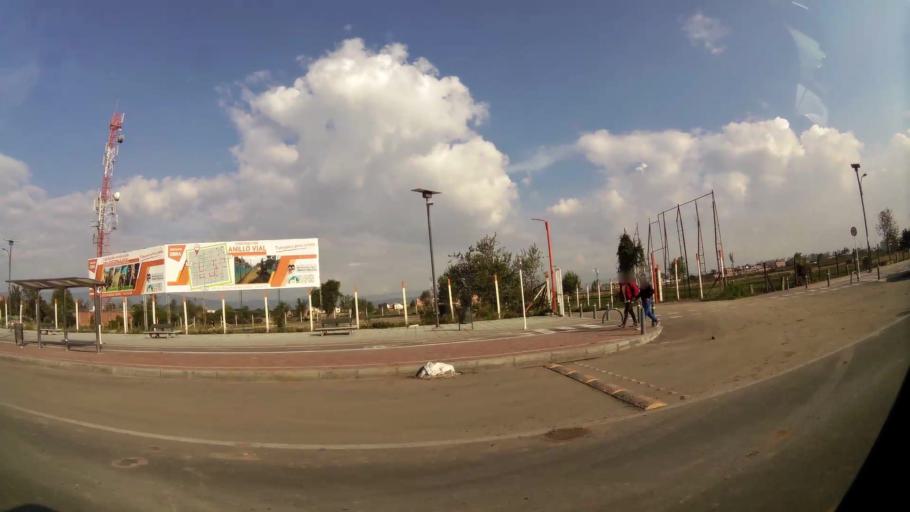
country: CO
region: Cundinamarca
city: Cota
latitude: 4.8062
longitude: -74.1050
